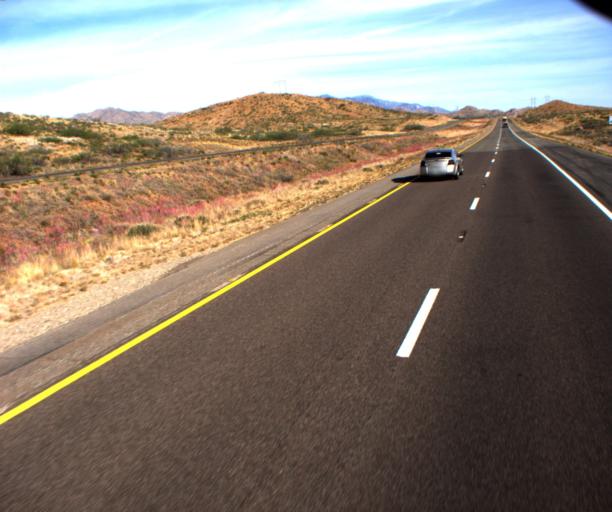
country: US
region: Arizona
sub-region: Cochise County
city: Willcox
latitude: 32.4586
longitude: -109.6661
